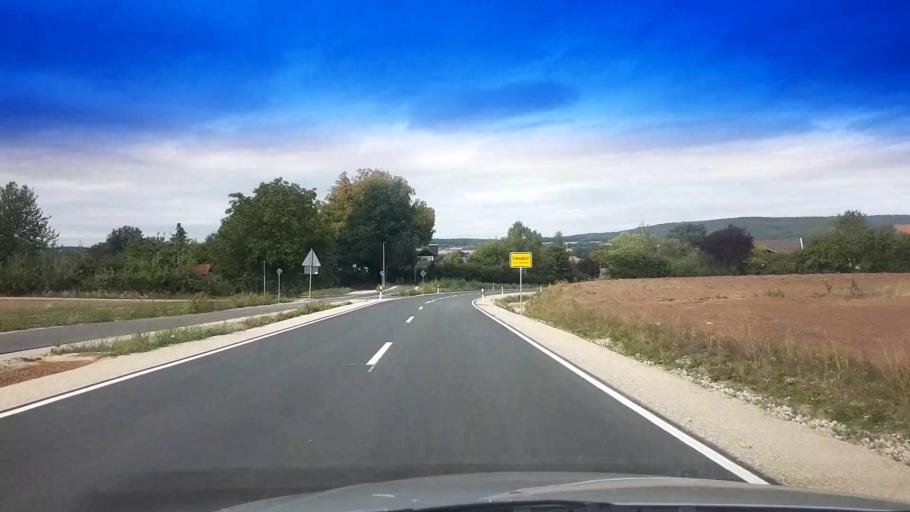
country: DE
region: Bavaria
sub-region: Upper Franconia
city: Frensdorf
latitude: 49.8116
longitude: 10.8709
